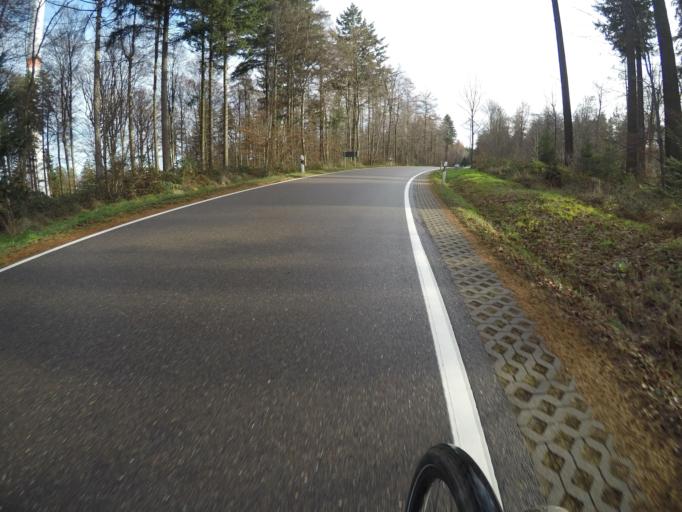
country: DE
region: Baden-Wuerttemberg
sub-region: Regierungsbezirk Stuttgart
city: Winterbach
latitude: 48.7776
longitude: 9.4650
